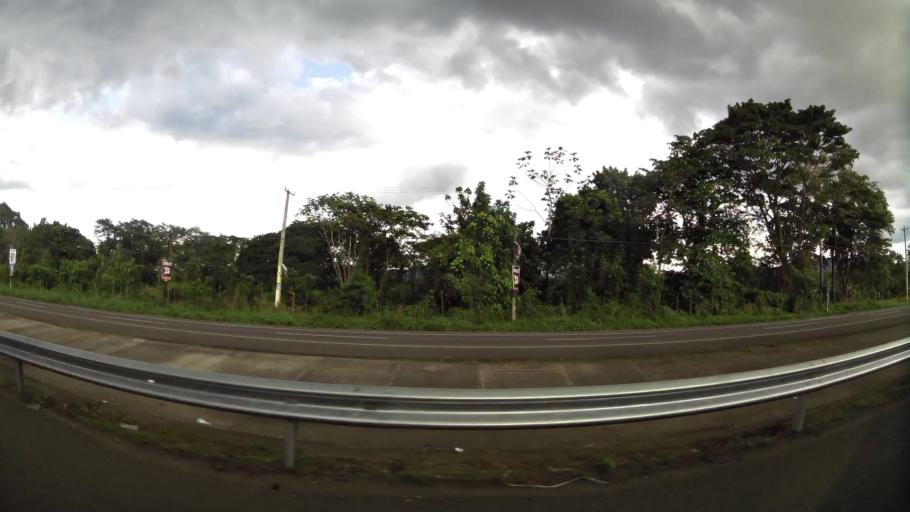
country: DO
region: Monsenor Nouel
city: Sabana del Puerto
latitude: 19.0194
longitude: -70.4457
